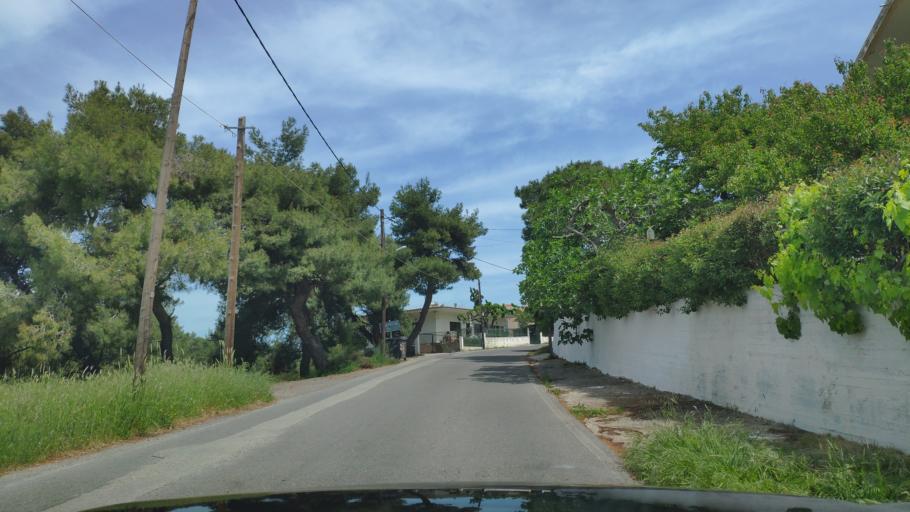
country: GR
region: Attica
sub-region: Nomarchia Anatolikis Attikis
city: Varnavas
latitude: 38.2202
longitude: 23.9185
